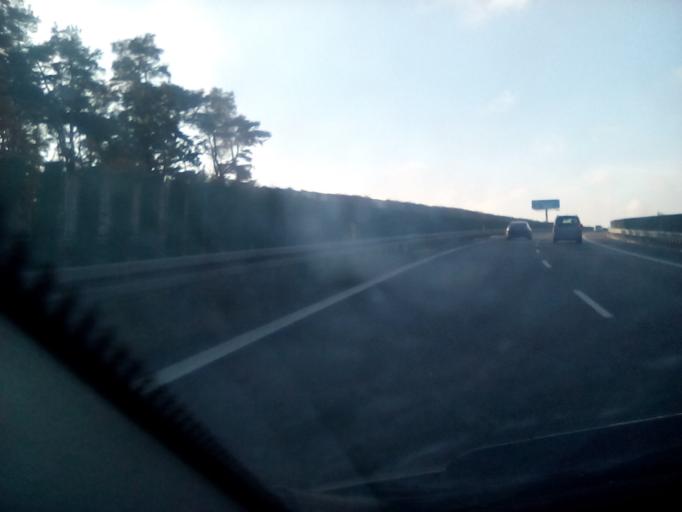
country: PL
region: Masovian Voivodeship
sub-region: Powiat grojecki
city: Grojec
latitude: 51.8963
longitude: 20.8605
